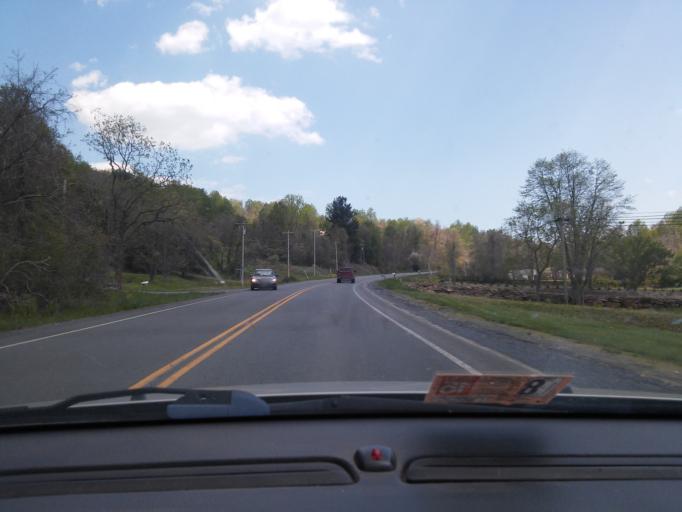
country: US
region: Virginia
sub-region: Warren County
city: Apple Mountain Lake
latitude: 38.8698
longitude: -78.1379
